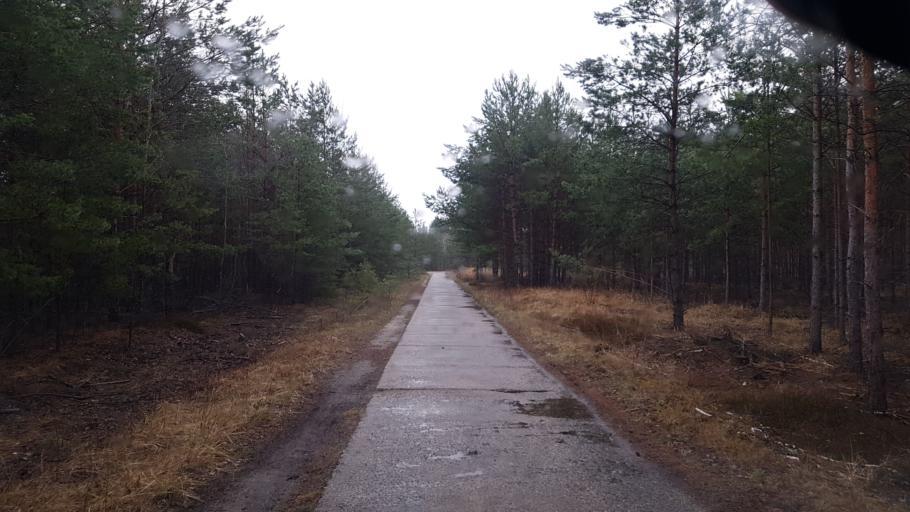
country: DE
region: Brandenburg
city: Grossraschen
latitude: 51.6023
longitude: 13.9909
